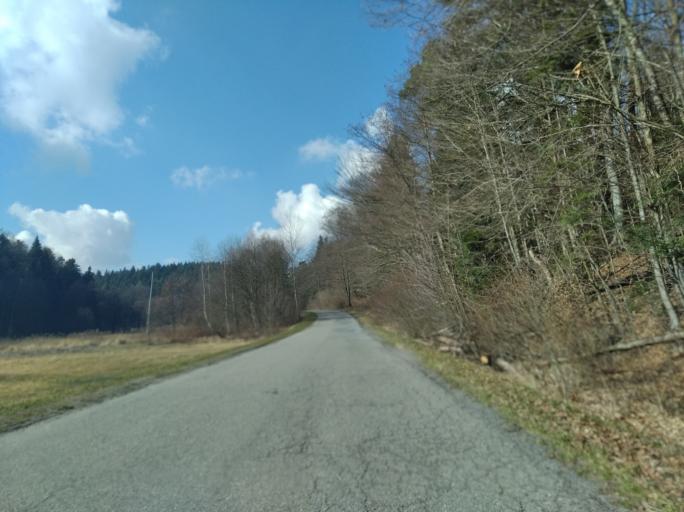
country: PL
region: Subcarpathian Voivodeship
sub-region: Powiat strzyzowski
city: Frysztak
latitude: 49.8663
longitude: 21.5562
